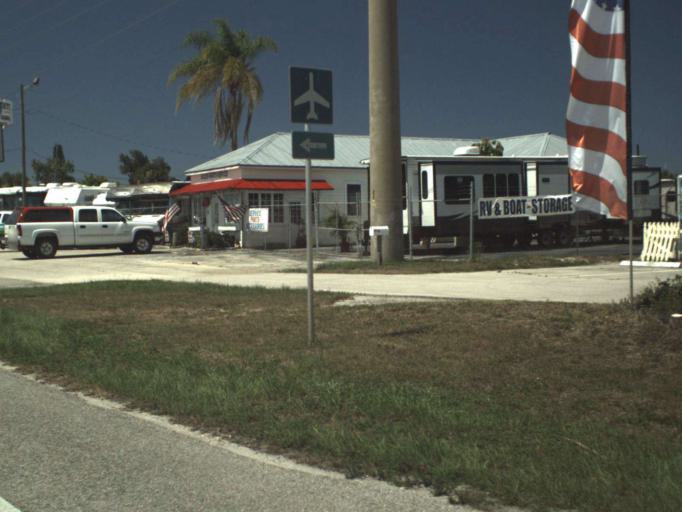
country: US
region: Florida
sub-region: Saint Lucie County
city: Fort Pierce North
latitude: 27.4828
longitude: -80.3402
